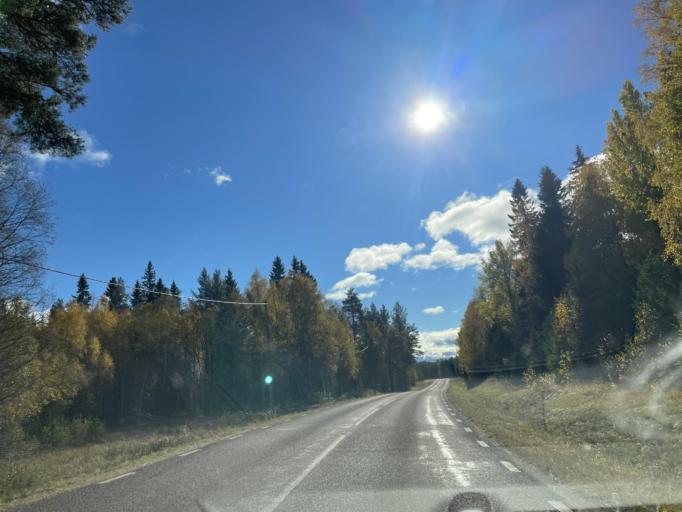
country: NO
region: Hedmark
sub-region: Trysil
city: Innbygda
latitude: 61.4579
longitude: 13.0937
